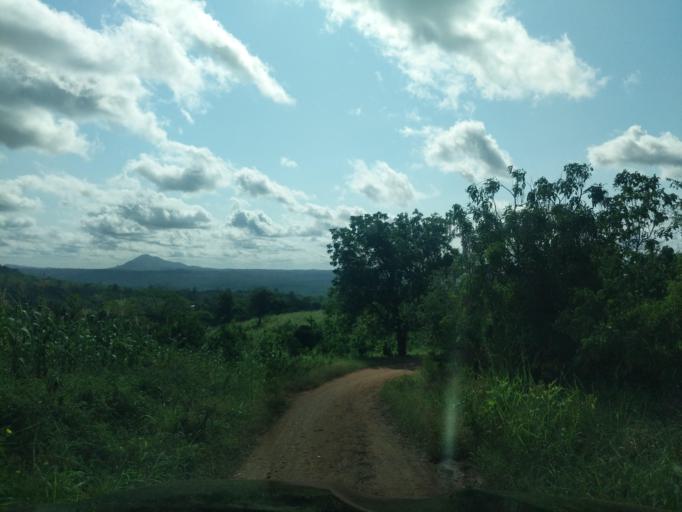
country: TZ
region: Tanga
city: Muheza
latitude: -5.4212
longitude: 38.6402
